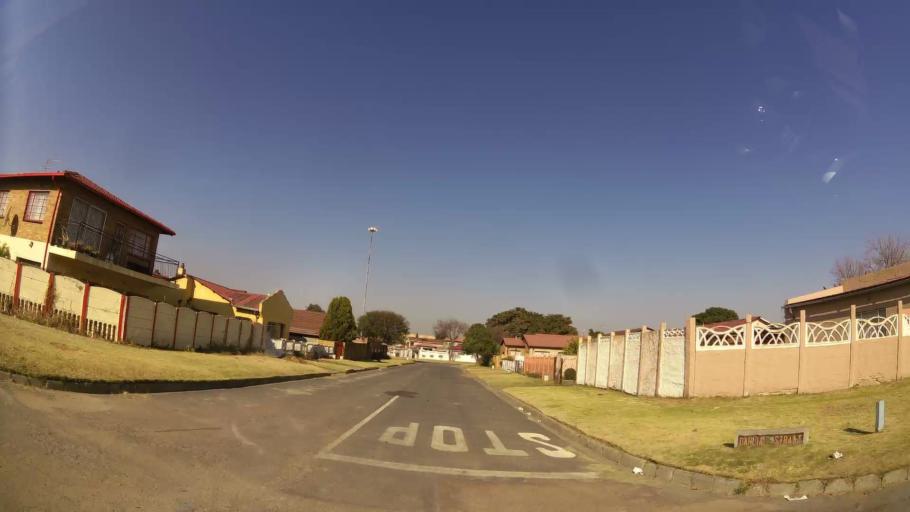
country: ZA
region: Gauteng
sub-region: Ekurhuleni Metropolitan Municipality
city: Boksburg
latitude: -26.2269
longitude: 28.2354
